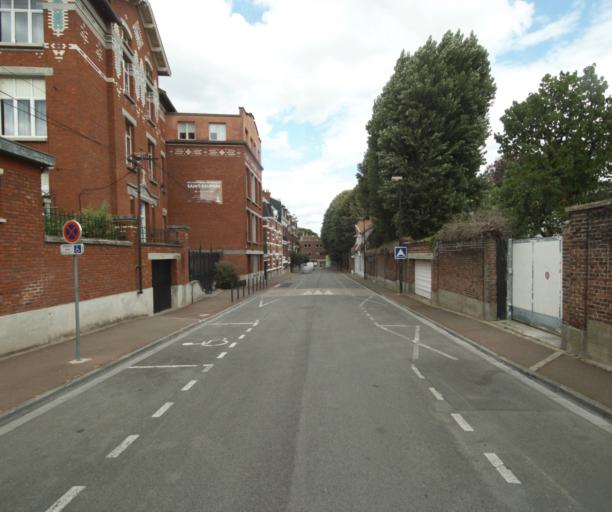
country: FR
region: Nord-Pas-de-Calais
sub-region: Departement du Nord
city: Roubaix
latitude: 50.6842
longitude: 3.1680
